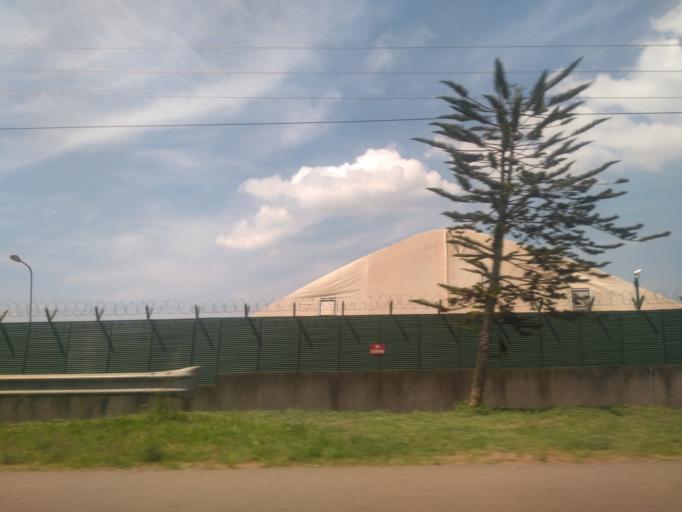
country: UG
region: Central Region
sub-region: Wakiso District
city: Entebbe
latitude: 0.0481
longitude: 32.4568
